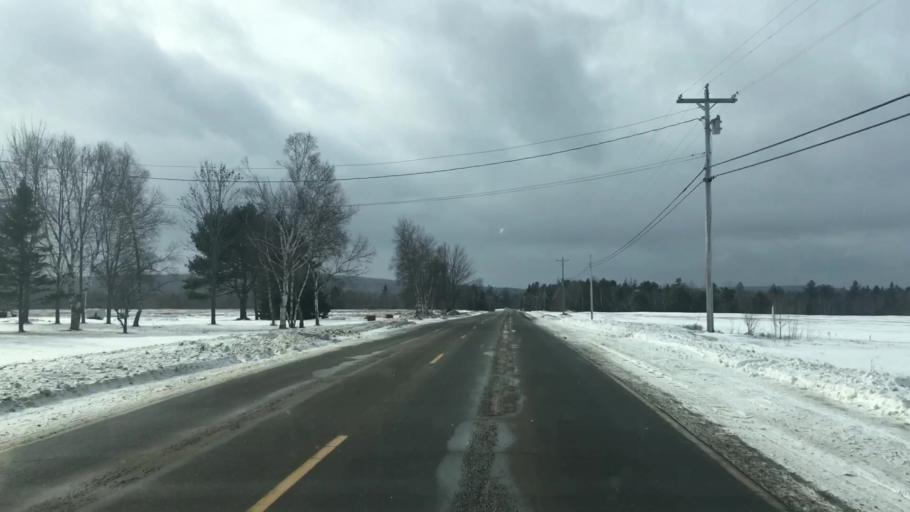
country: US
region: Maine
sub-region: Washington County
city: Calais
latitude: 45.0226
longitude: -67.3782
